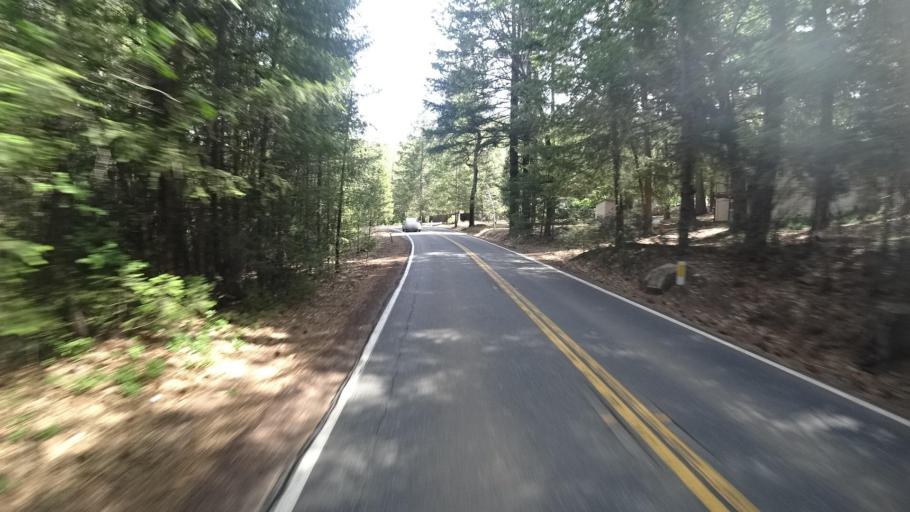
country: US
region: California
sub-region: Lake County
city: Cobb
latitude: 38.8683
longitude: -122.7185
